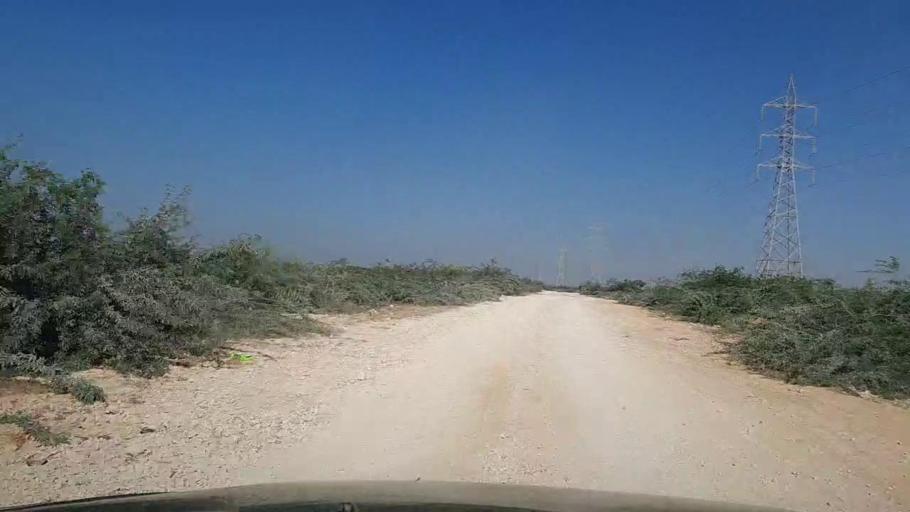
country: PK
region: Sindh
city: Thatta
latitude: 24.6268
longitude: 67.8344
